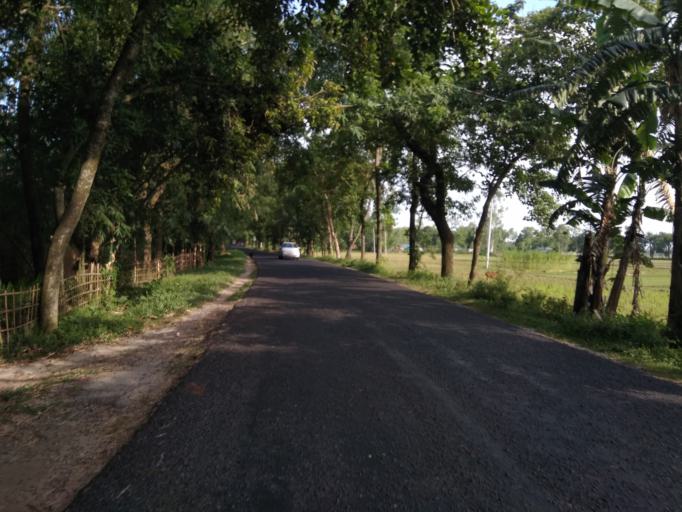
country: BD
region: Rangpur Division
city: Rangpur
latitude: 25.8346
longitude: 89.1159
